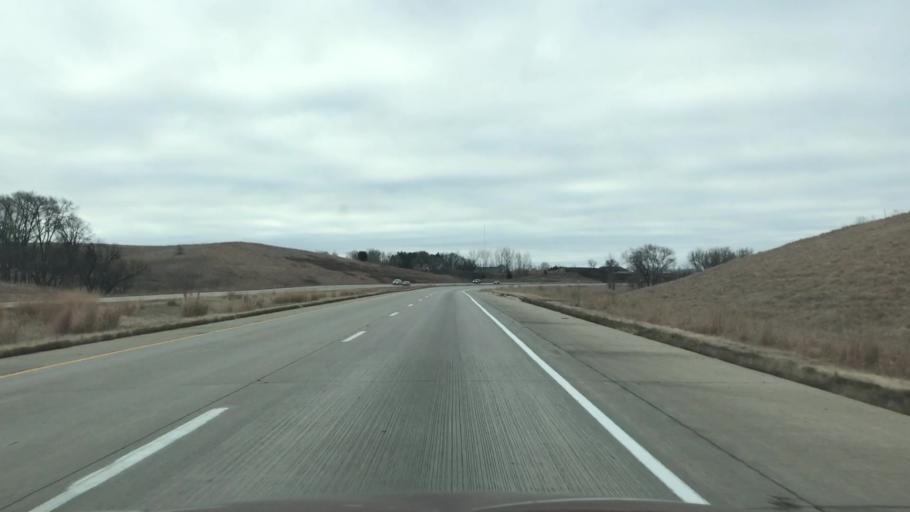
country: US
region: Iowa
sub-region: Woodbury County
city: Sioux City
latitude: 42.5022
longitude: -96.3225
